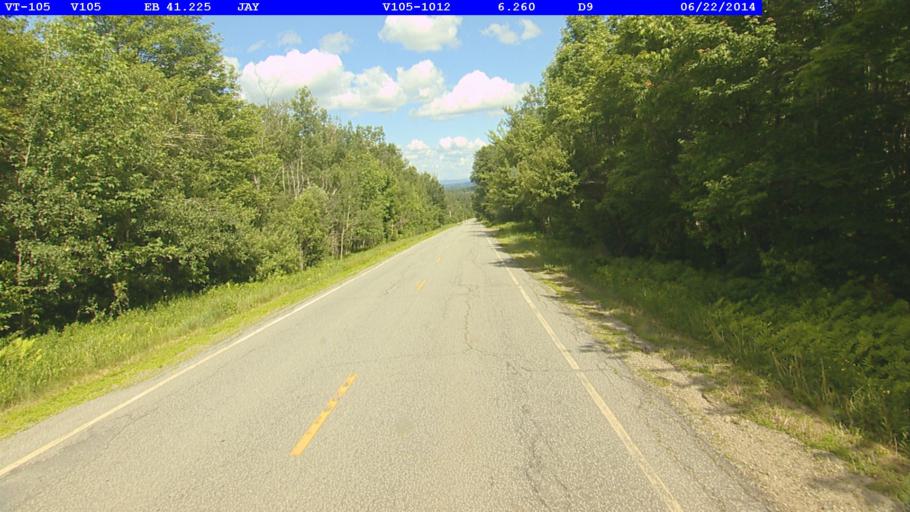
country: CA
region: Quebec
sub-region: Monteregie
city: Sutton
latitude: 44.9728
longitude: -72.4625
